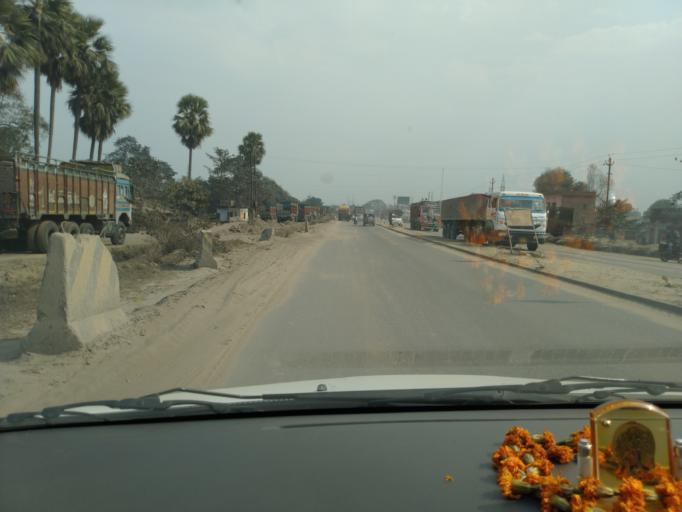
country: IN
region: Bihar
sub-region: Rohtas
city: Dehri
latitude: 24.9131
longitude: 84.1635
